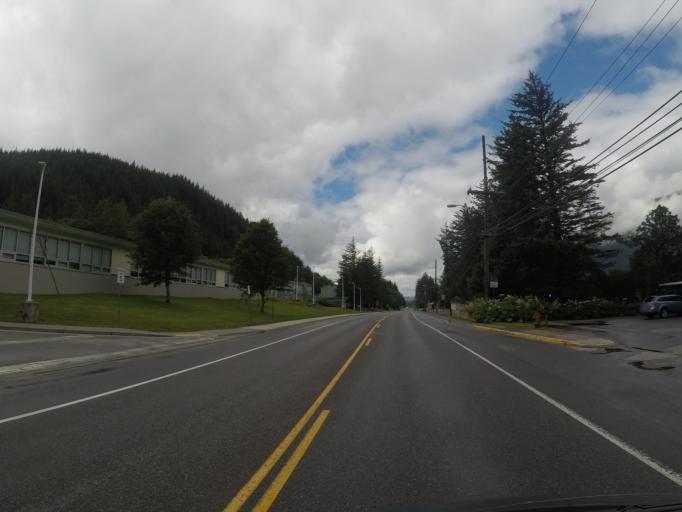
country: US
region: Alaska
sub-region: Juneau City and Borough
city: Juneau
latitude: 58.2823
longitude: -134.4031
